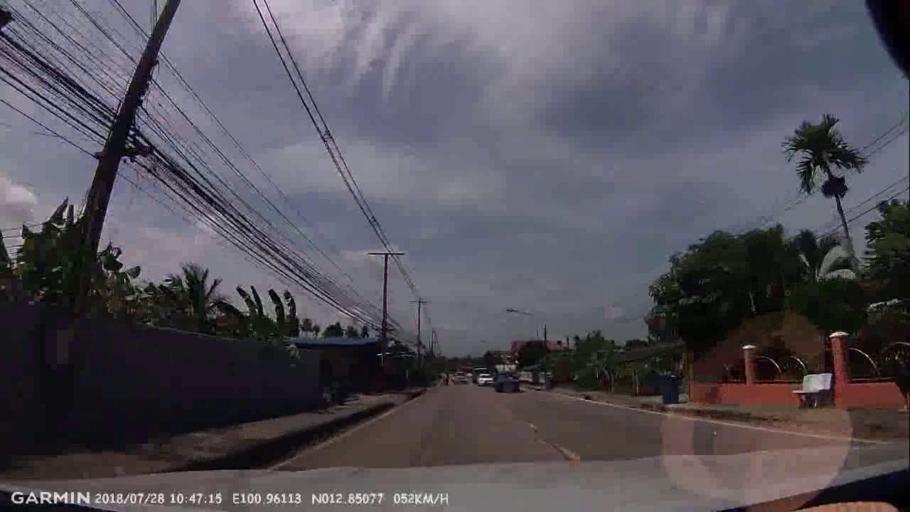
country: TH
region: Chon Buri
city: Phatthaya
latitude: 12.8508
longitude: 100.9611
